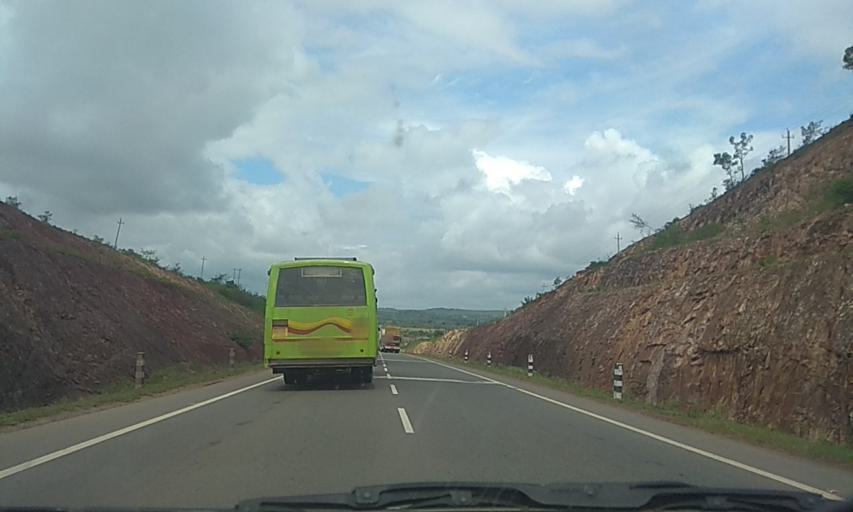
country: IN
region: Karnataka
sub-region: Dharwad
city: Hubli
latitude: 15.4018
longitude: 74.9964
